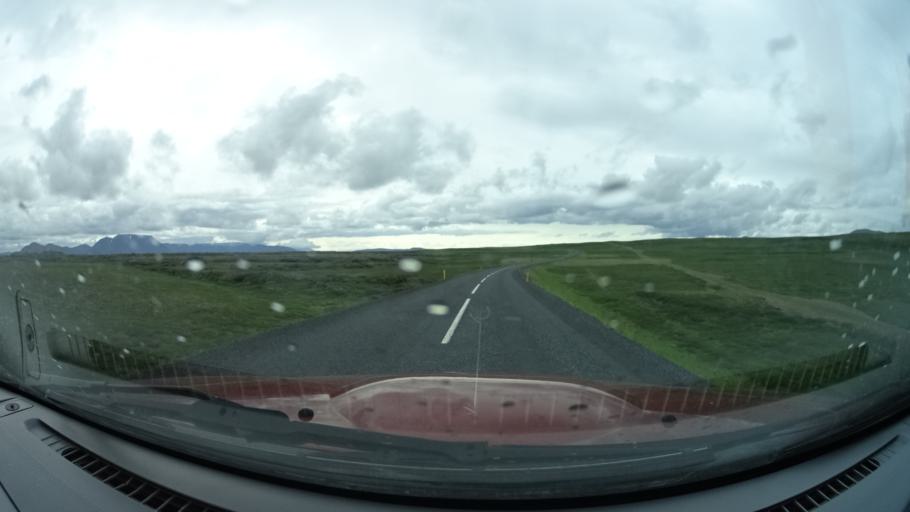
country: IS
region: Northeast
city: Laugar
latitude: 65.6563
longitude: -16.5842
